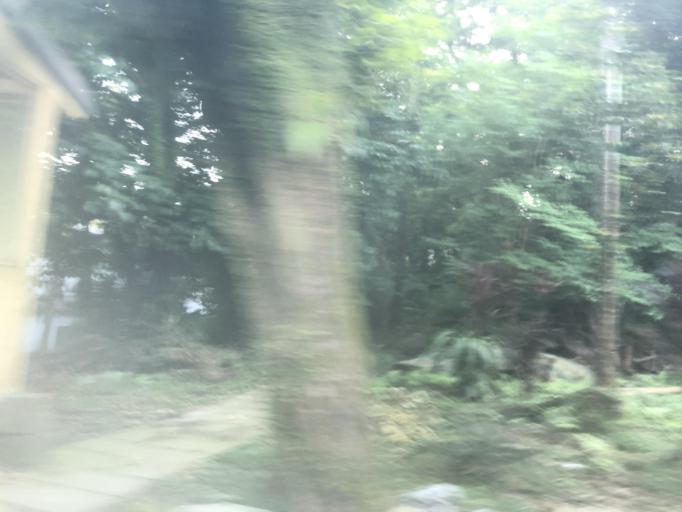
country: TW
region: Taiwan
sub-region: Keelung
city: Keelung
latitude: 25.1758
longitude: 121.6551
